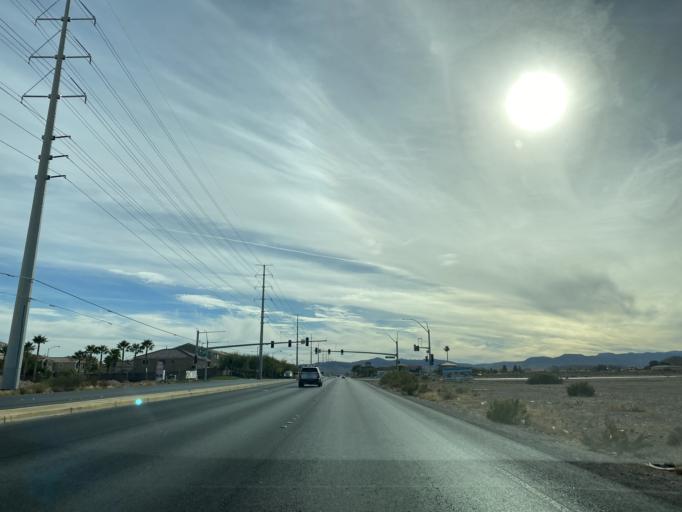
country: US
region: Nevada
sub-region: Clark County
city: Enterprise
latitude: 36.0351
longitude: -115.2434
